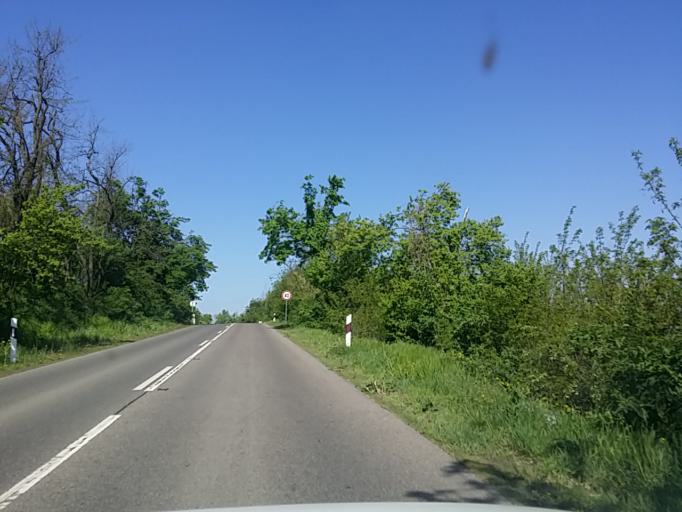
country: HU
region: Pest
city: Kerepes
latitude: 47.5919
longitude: 19.2914
